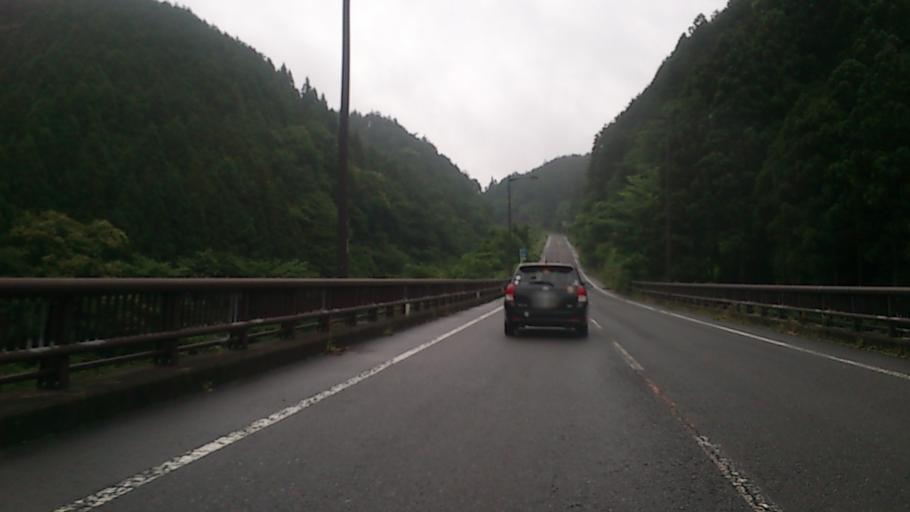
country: JP
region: Tochigi
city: Karasuyama
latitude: 36.6926
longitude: 140.2191
